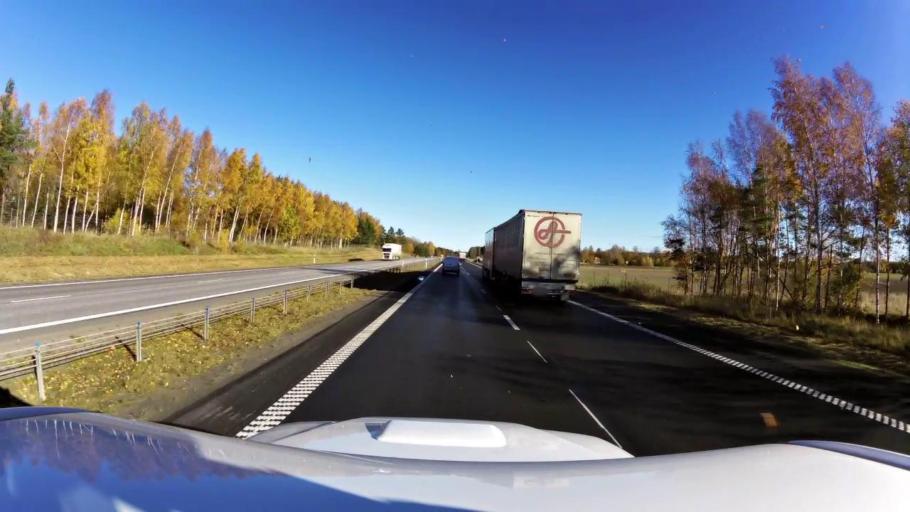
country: SE
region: OEstergoetland
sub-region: Linkopings Kommun
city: Vikingstad
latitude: 58.3967
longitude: 15.4270
